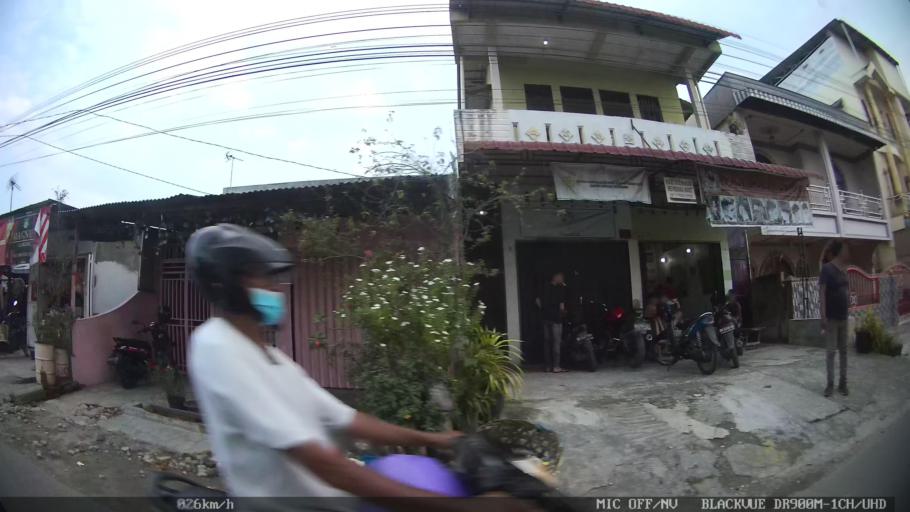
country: ID
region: North Sumatra
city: Medan
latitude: 3.6068
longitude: 98.7032
